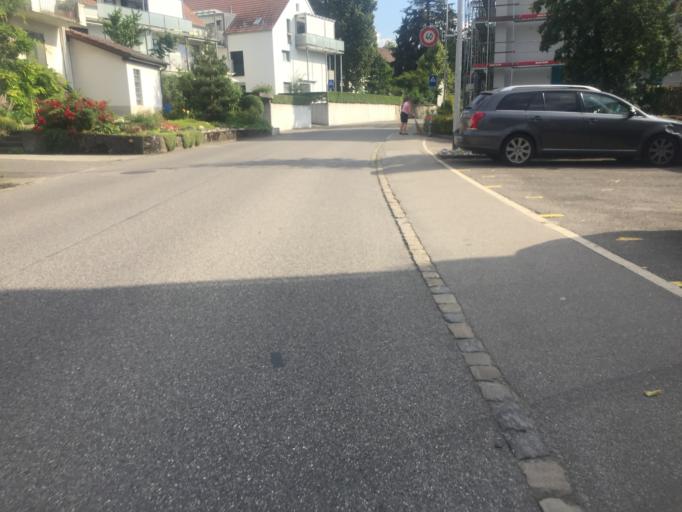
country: CH
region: Bern
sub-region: Bern-Mittelland District
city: Bolligen
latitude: 46.9599
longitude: 7.4952
